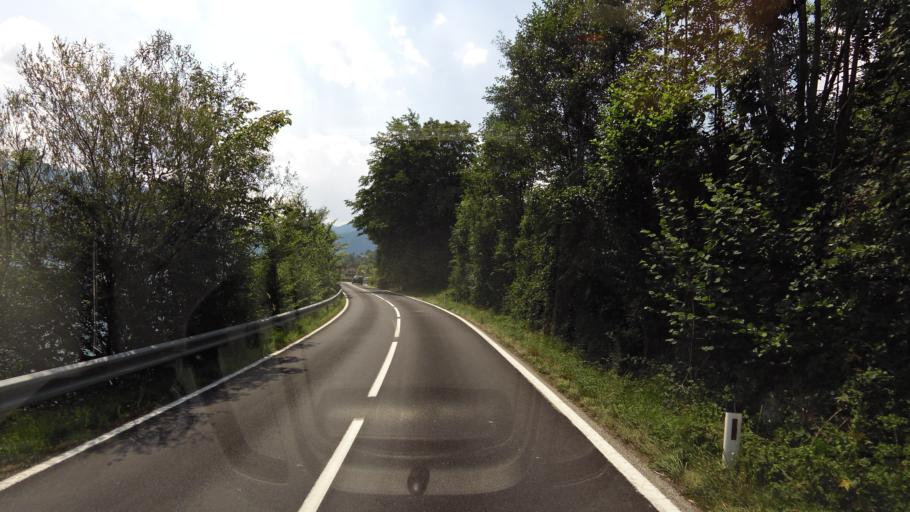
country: AT
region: Upper Austria
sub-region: Politischer Bezirk Vocklabruck
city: Steinbach am Attersee
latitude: 47.8251
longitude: 13.5128
